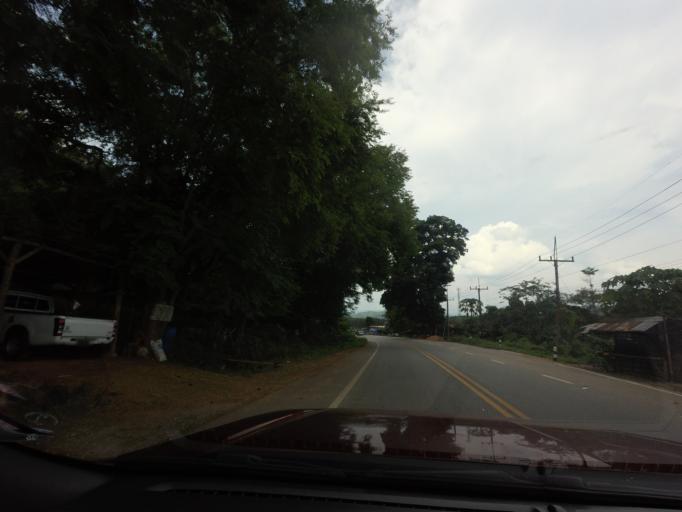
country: TH
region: Yala
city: Ban Nang Sata
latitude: 6.2338
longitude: 101.2111
